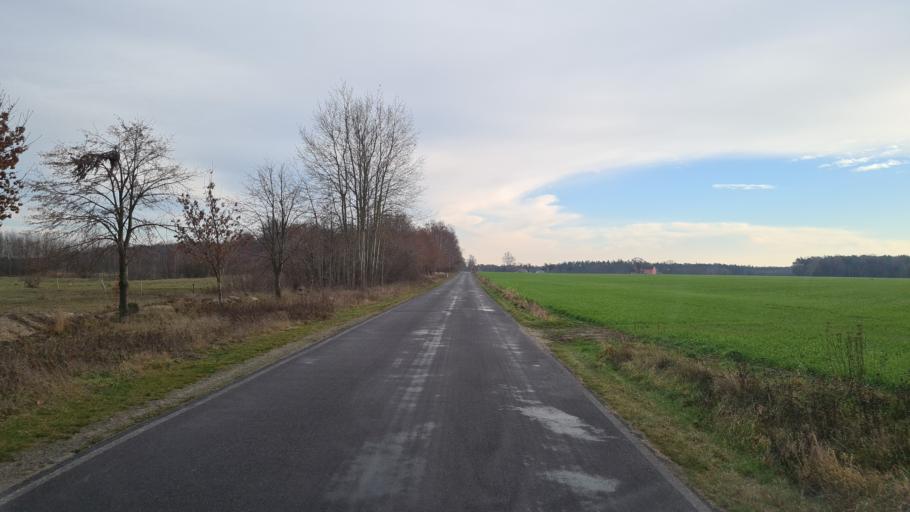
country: DE
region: Brandenburg
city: Finsterwalde
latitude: 51.6069
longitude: 13.7199
